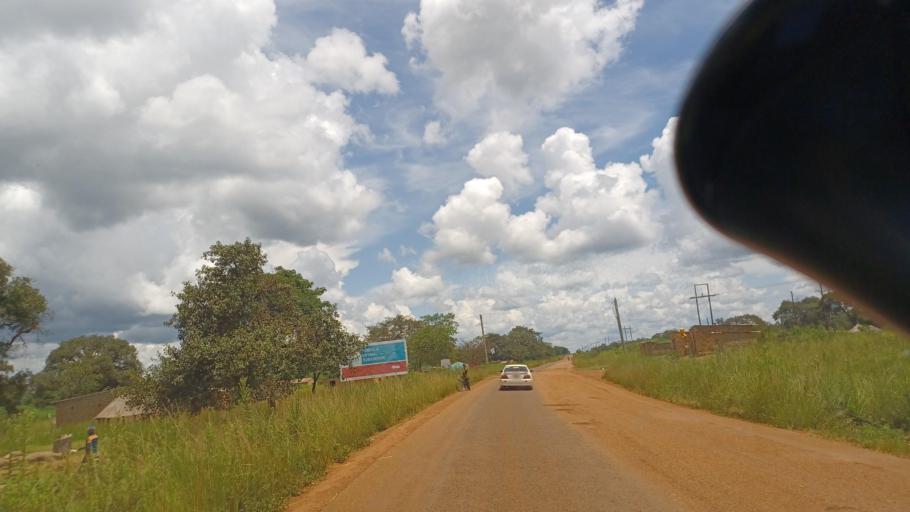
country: ZM
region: North-Western
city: Solwezi
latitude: -12.4823
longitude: 26.1973
